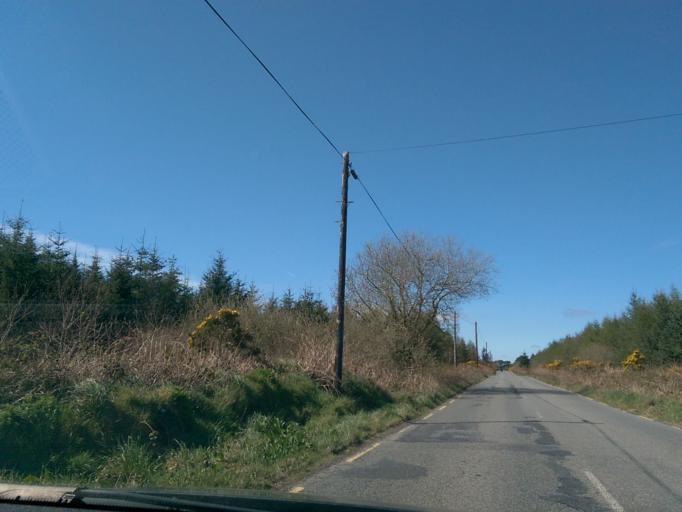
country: IE
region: Leinster
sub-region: Wicklow
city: Carnew
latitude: 52.8235
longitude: -6.5150
